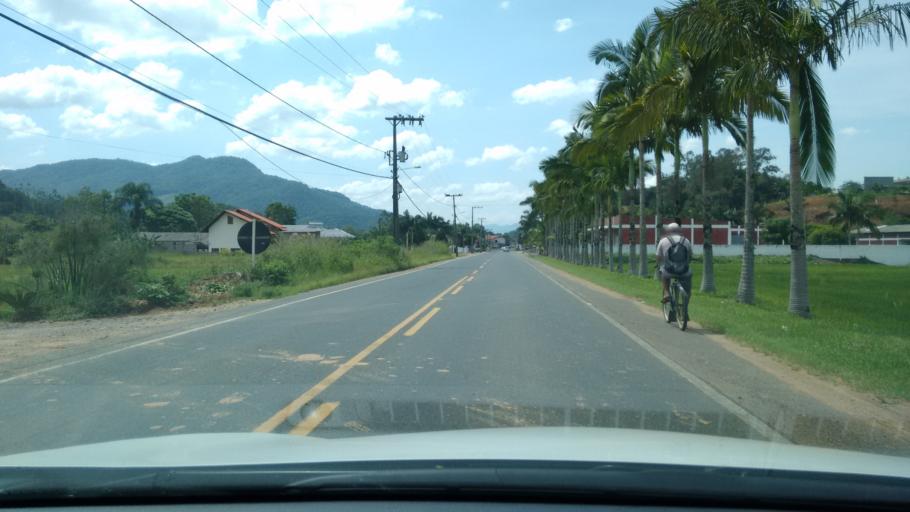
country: BR
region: Santa Catarina
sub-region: Timbo
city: Timbo
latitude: -26.8513
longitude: -49.3298
